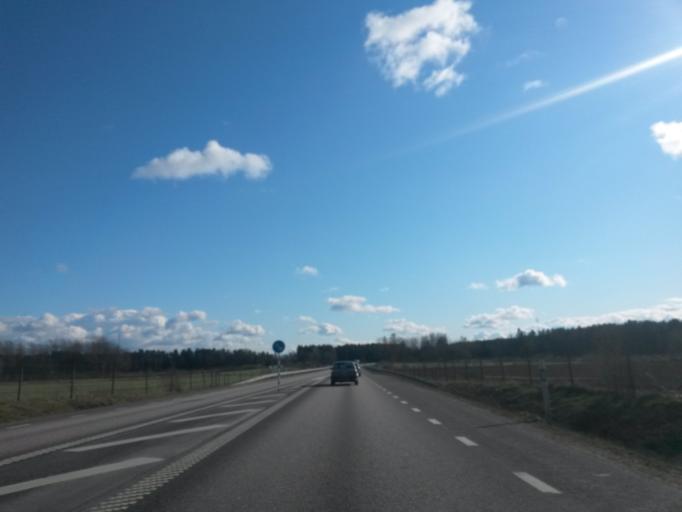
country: SE
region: Vaestra Goetaland
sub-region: Vara Kommun
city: Vara
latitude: 58.1697
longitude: 12.8881
